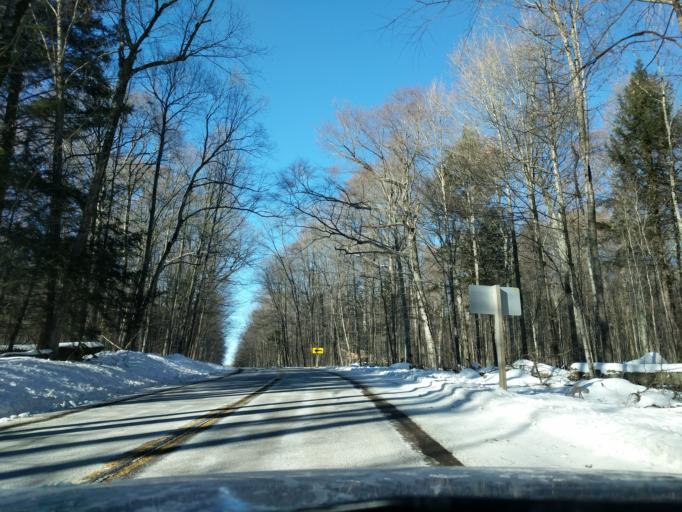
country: US
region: Wisconsin
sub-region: Menominee County
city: Keshena
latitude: 45.0895
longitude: -88.6273
